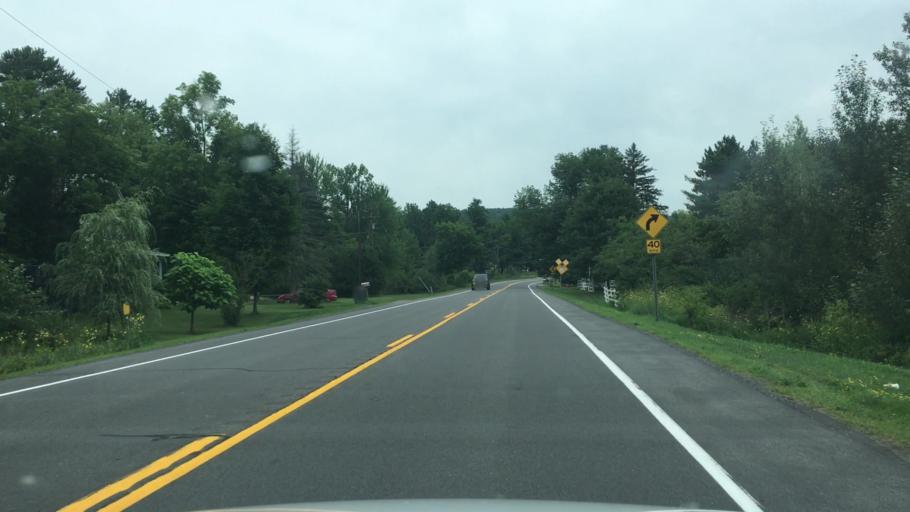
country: US
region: New York
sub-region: Essex County
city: Keeseville
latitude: 44.4629
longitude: -73.5998
